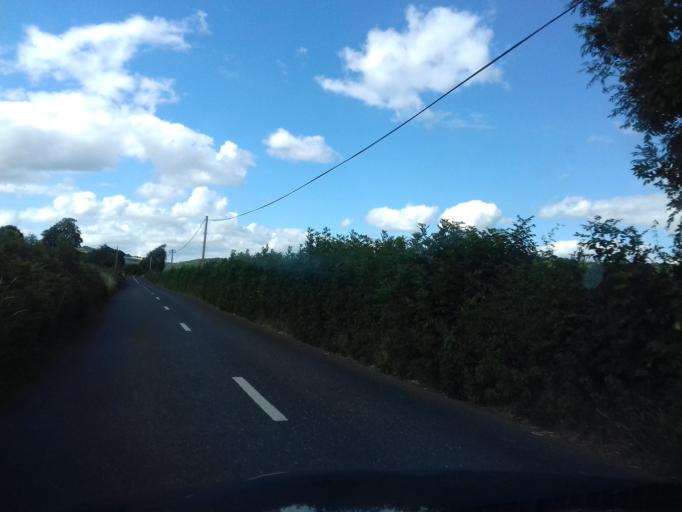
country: IE
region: Munster
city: Carrick-on-Suir
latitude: 52.3806
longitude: -7.4567
